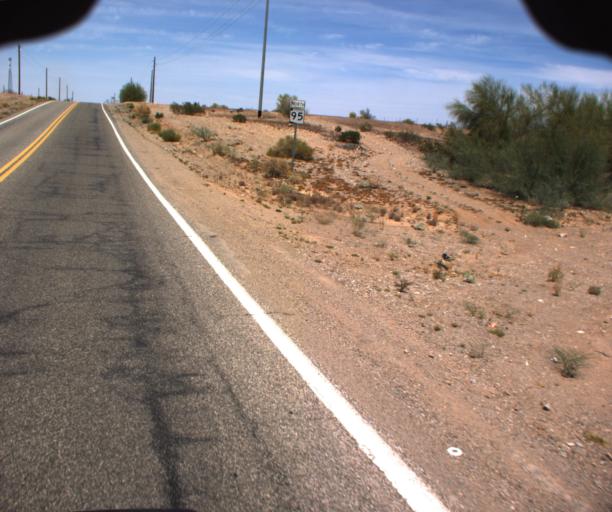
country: US
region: Arizona
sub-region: La Paz County
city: Quartzsite
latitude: 33.6928
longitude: -114.2170
